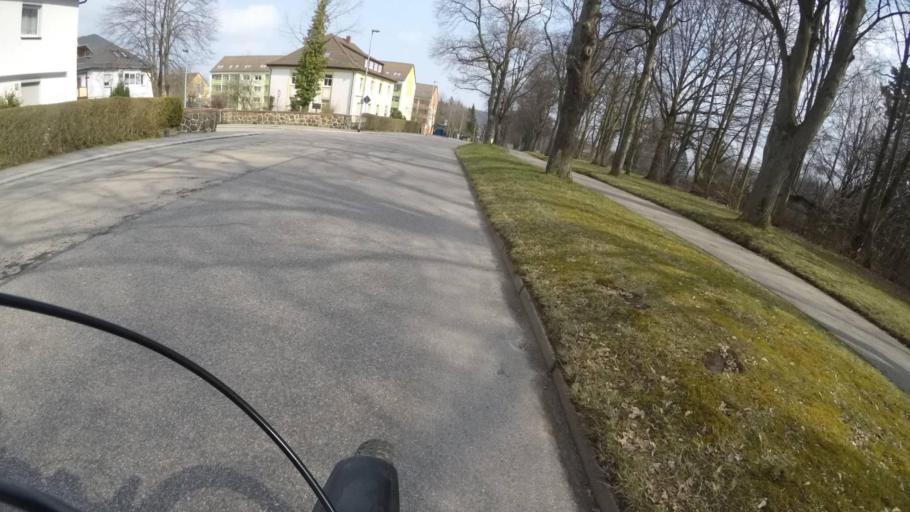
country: DE
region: Saxony
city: Limbach-Oberfrohna
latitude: 50.8657
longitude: 12.7469
